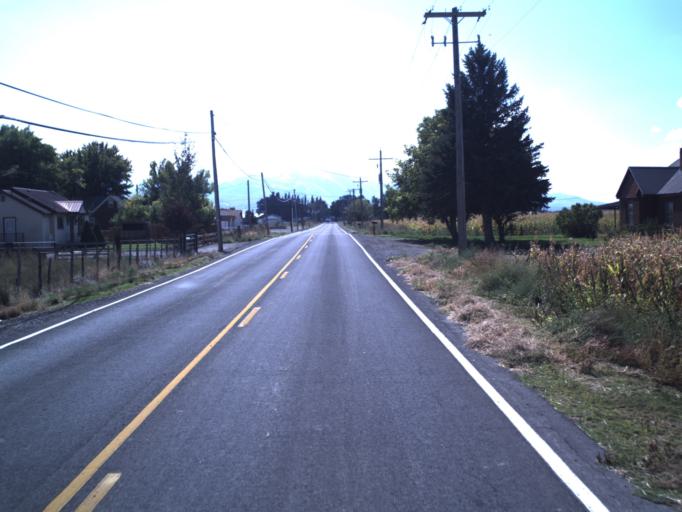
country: US
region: Utah
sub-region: Utah County
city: Benjamin
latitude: 40.1211
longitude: -111.7305
